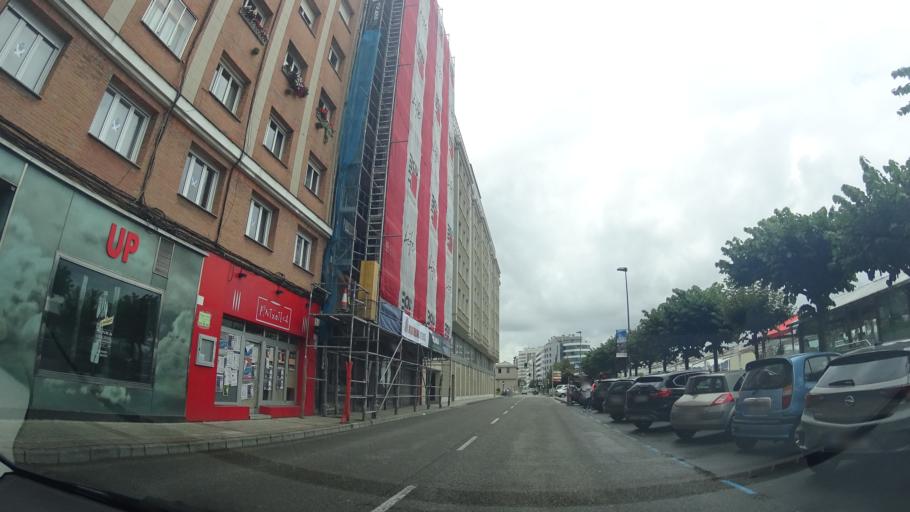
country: ES
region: Asturias
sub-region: Province of Asturias
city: Gijon
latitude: 43.5418
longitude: -5.6702
